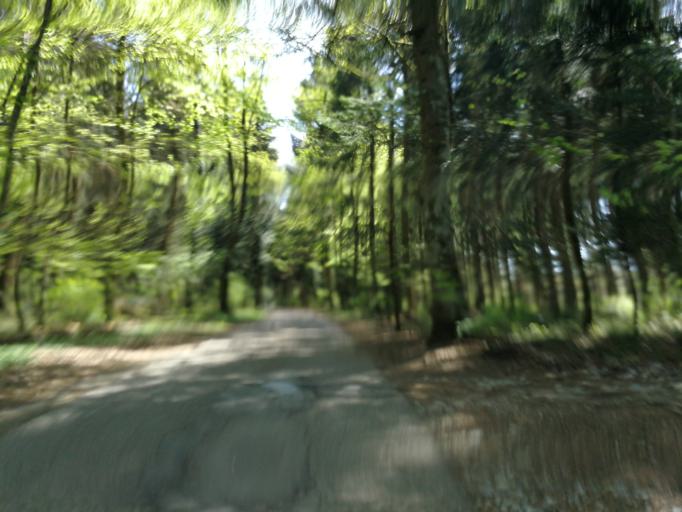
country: CH
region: Zurich
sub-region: Bezirk Hinwil
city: Hinwil
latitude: 47.2987
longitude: 8.8207
